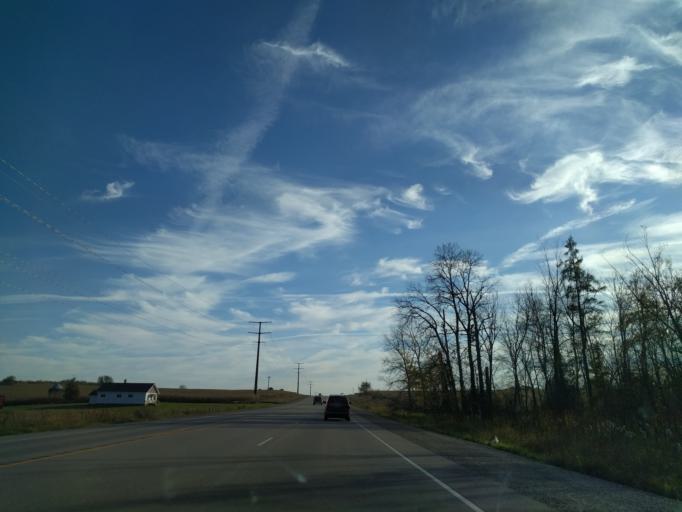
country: US
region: Wisconsin
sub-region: Marinette County
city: Peshtigo
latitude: 45.2739
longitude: -87.9907
